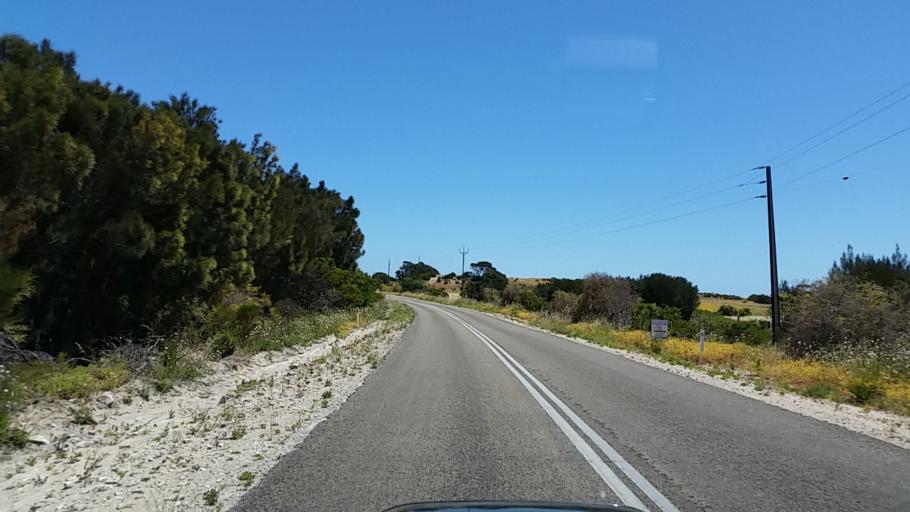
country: AU
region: South Australia
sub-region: Yorke Peninsula
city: Honiton
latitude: -35.2248
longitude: 136.9900
